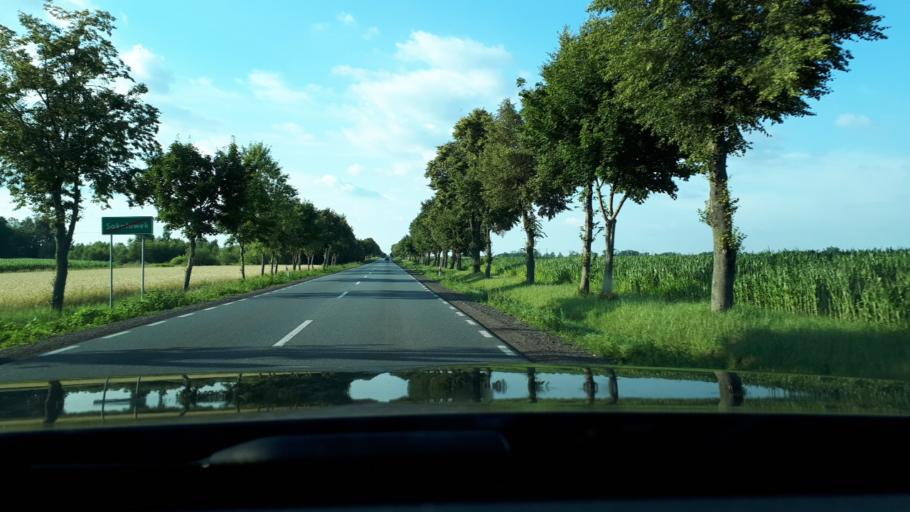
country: PL
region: Masovian Voivodeship
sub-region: Powiat ciechanowski
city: Ciechanow
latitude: 52.8330
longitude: 20.6191
